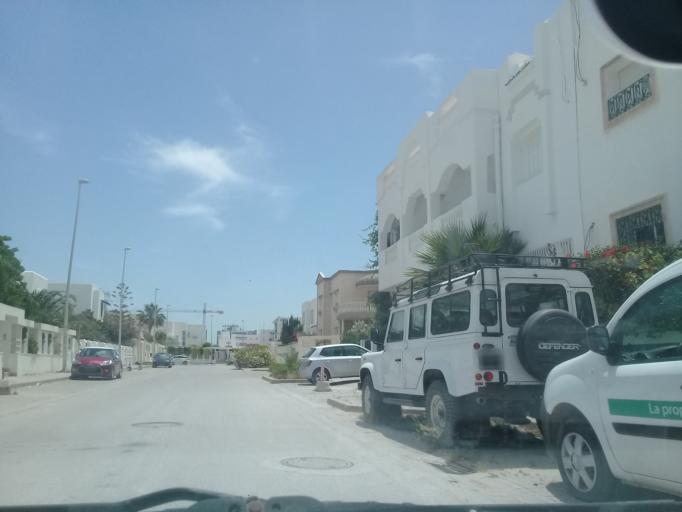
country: TN
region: Ariana
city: Ariana
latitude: 36.8350
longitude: 10.2312
